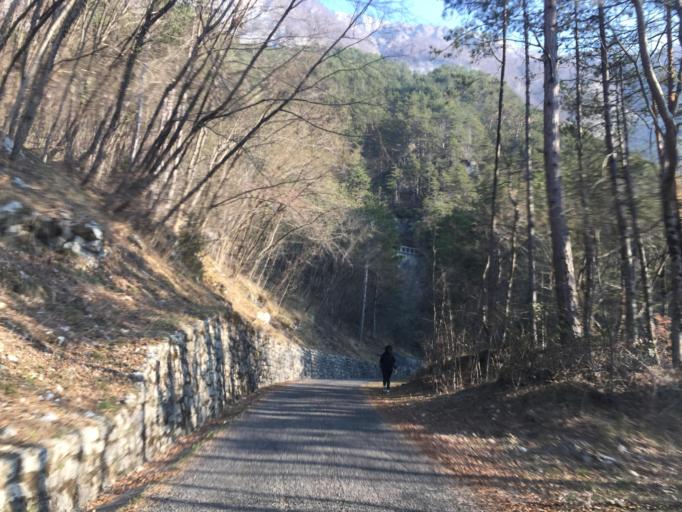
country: IT
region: Friuli Venezia Giulia
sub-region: Provincia di Udine
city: Amaro
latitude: 46.3839
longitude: 13.0838
